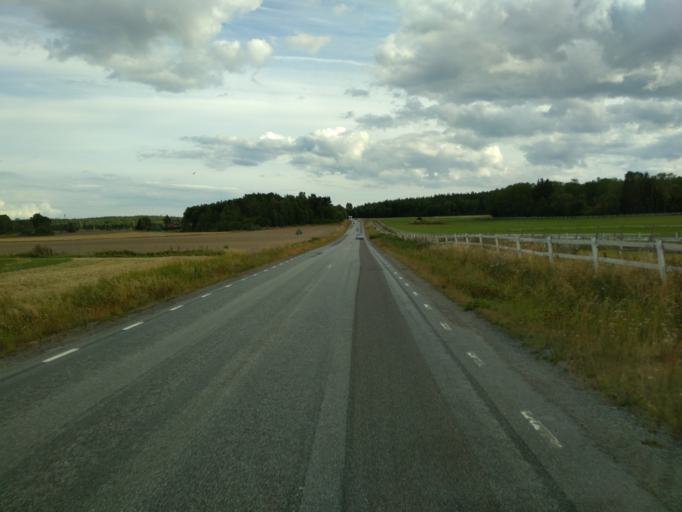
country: SE
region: Uppsala
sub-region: Habo Kommun
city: Balsta
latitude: 59.6603
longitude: 17.5556
